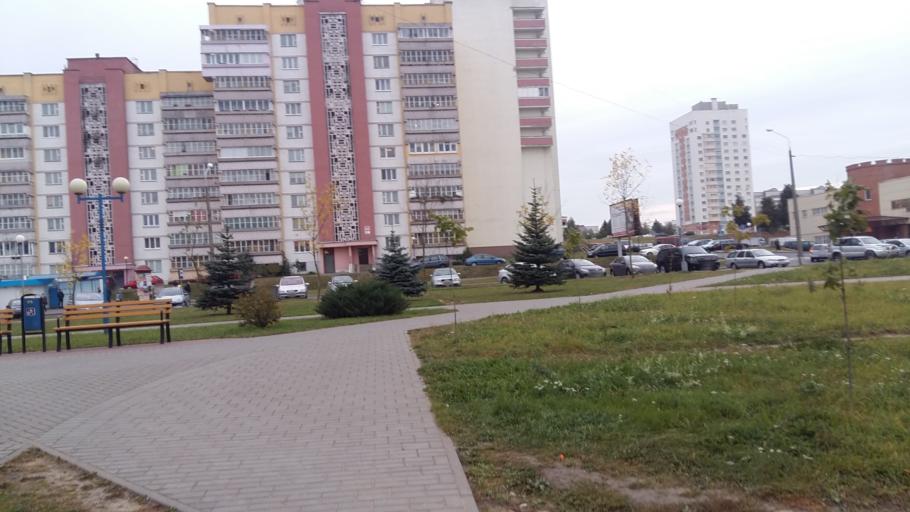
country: BY
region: Grodnenskaya
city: Hrodna
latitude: 53.7105
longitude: 23.8504
